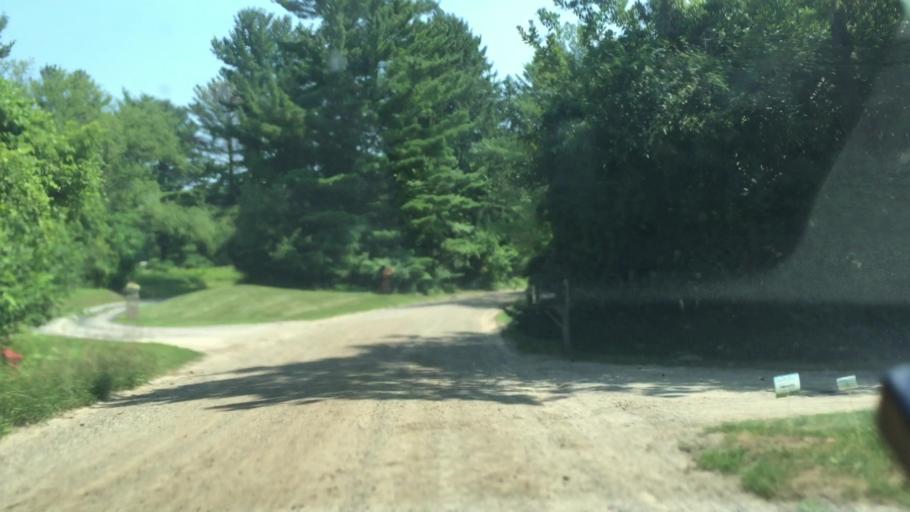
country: US
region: Michigan
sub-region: Oakland County
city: Orchard Lake
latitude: 42.5523
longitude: -83.3354
